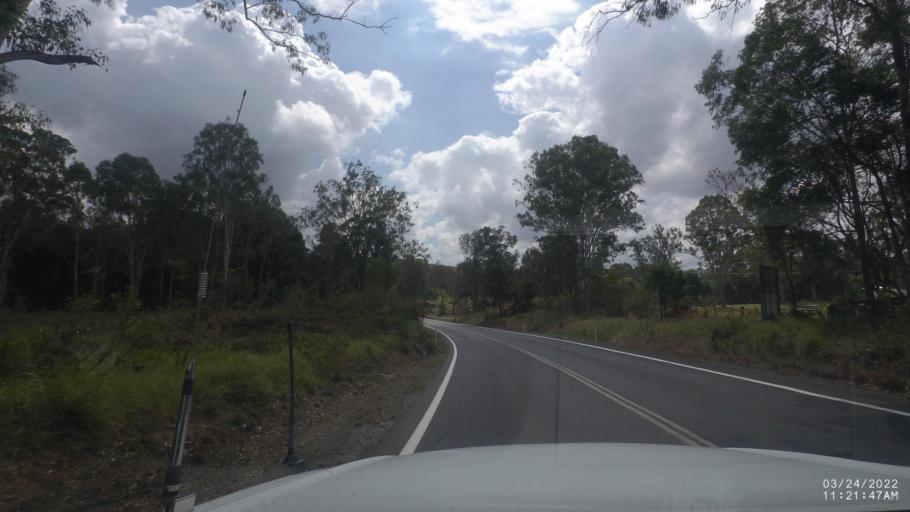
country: AU
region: Queensland
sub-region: Logan
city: Windaroo
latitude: -27.7980
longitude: 153.1773
